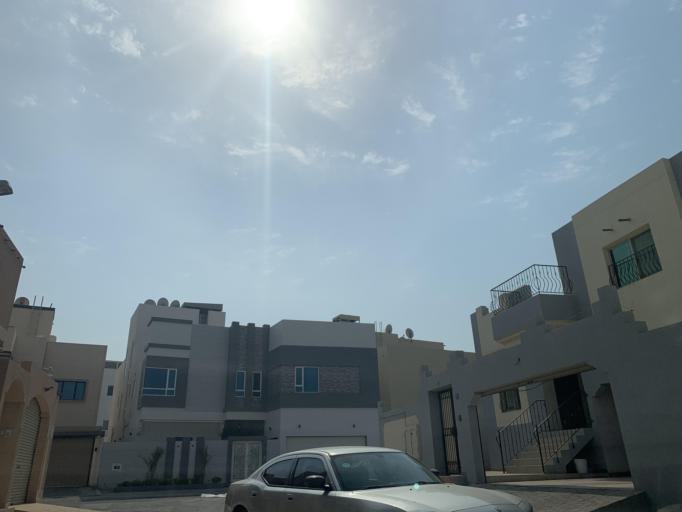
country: BH
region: Manama
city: Jidd Hafs
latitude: 26.2126
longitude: 50.4880
